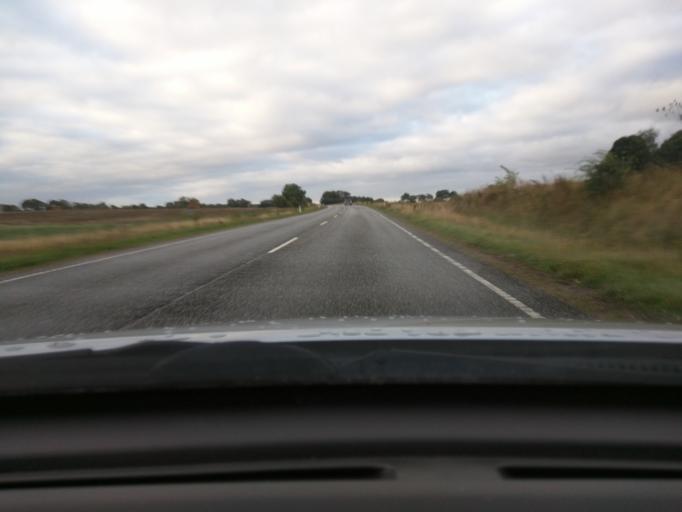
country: DK
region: Central Jutland
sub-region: Silkeborg Kommune
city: Kjellerup
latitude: 56.3118
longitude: 9.3273
